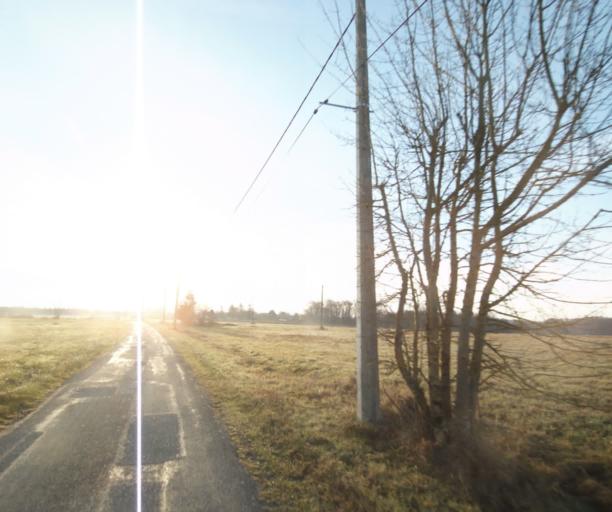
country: FR
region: Poitou-Charentes
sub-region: Departement de la Charente-Maritime
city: Fontcouverte
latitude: 45.7665
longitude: -0.5597
